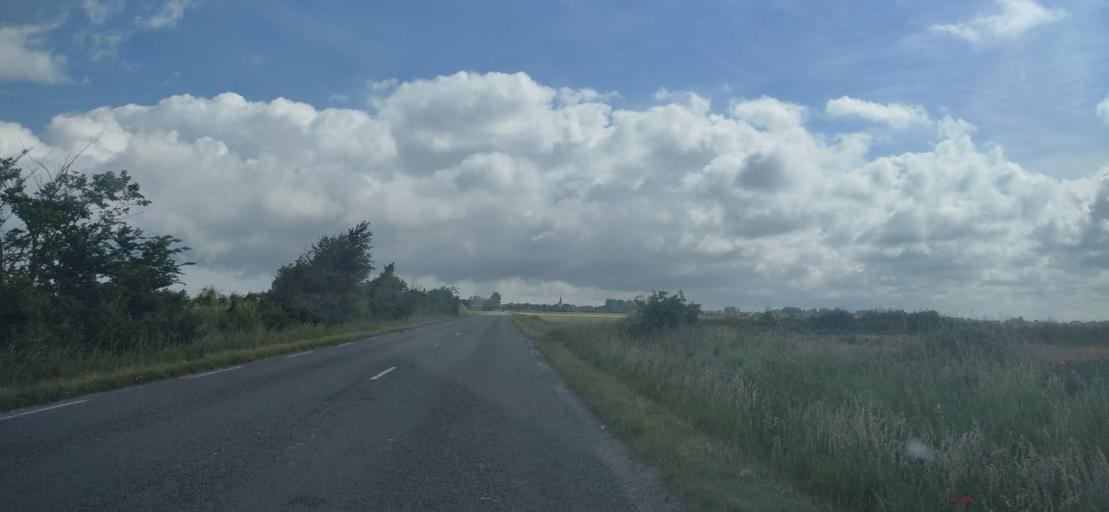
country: FR
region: Nord-Pas-de-Calais
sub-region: Departement du Pas-de-Calais
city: Oye-Plage
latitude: 50.9697
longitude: 2.0198
